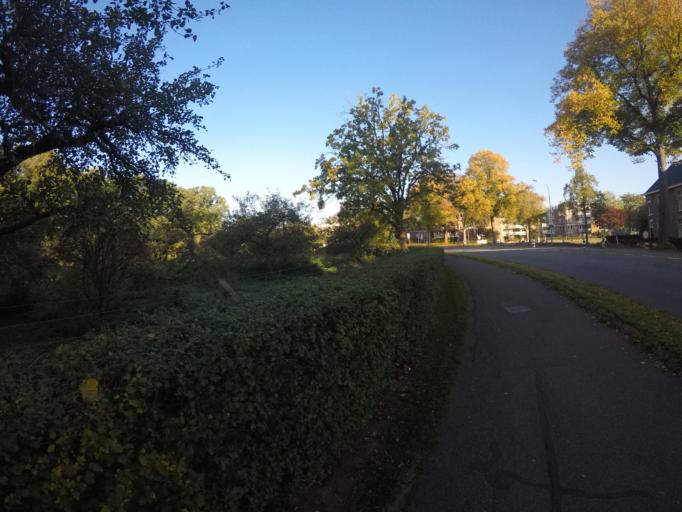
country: NL
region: Gelderland
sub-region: Gemeente Zevenaar
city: Zevenaar
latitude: 51.9275
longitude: 6.0801
